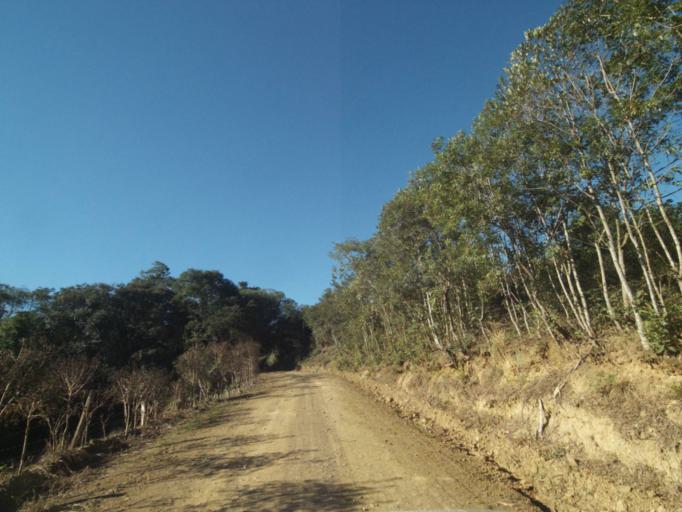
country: BR
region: Parana
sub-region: Tibagi
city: Tibagi
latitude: -24.5543
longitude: -50.5177
